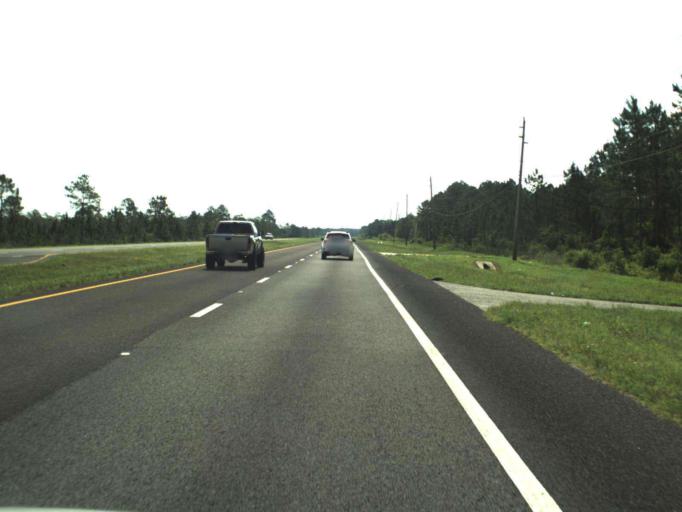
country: US
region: Florida
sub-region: Volusia County
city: Samsula-Spruce Creek
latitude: 29.0259
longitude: -81.1440
